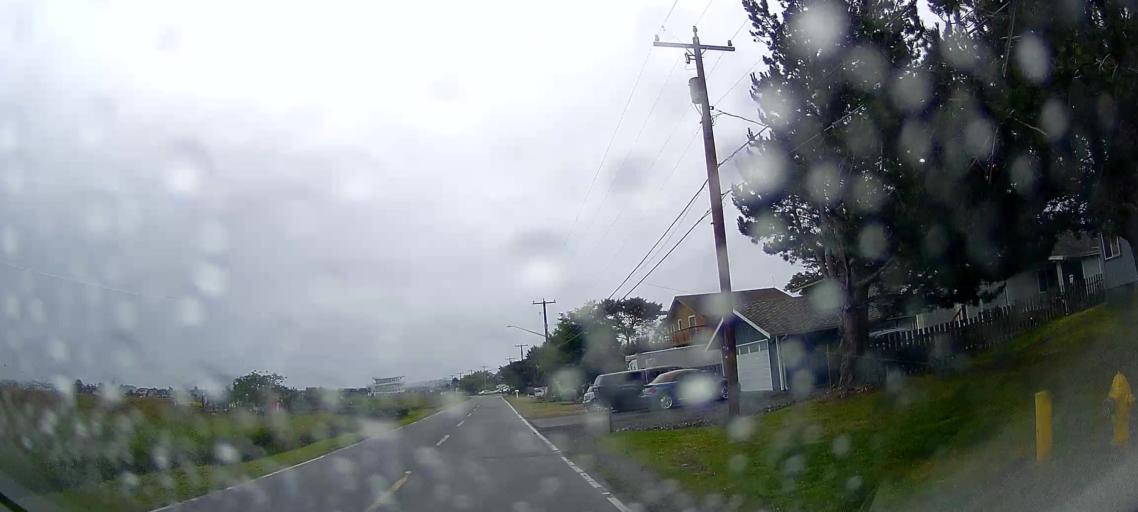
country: US
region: Washington
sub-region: Whatcom County
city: Birch Bay
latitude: 48.7955
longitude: -122.7106
